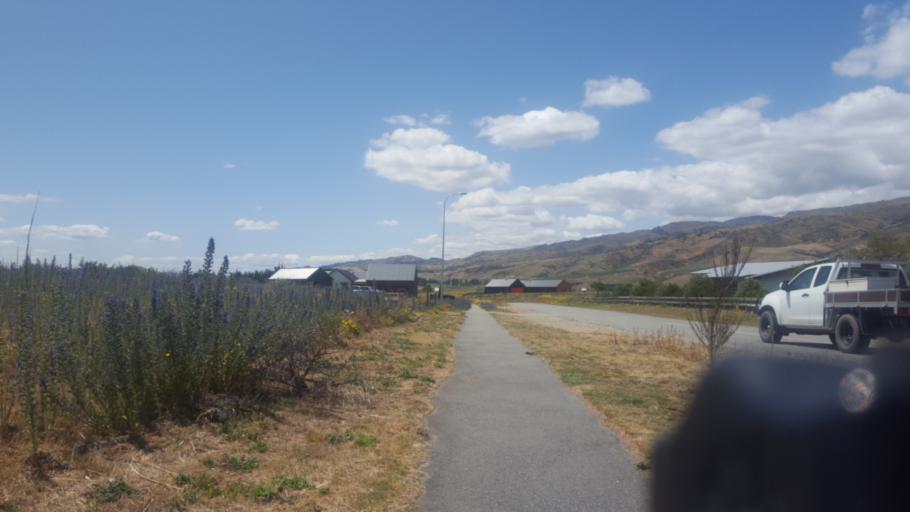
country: NZ
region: Otago
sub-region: Queenstown-Lakes District
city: Wanaka
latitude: -45.0306
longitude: 169.2038
